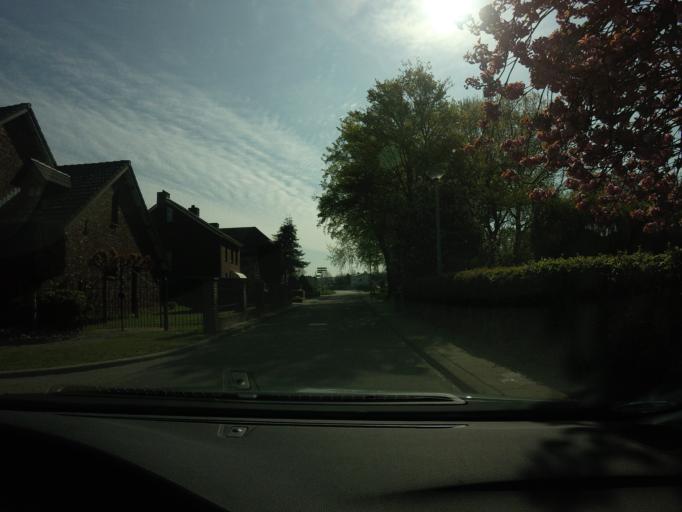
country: NL
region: Limburg
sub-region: Gemeente Maastricht
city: Heer
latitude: 50.8469
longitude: 5.7370
